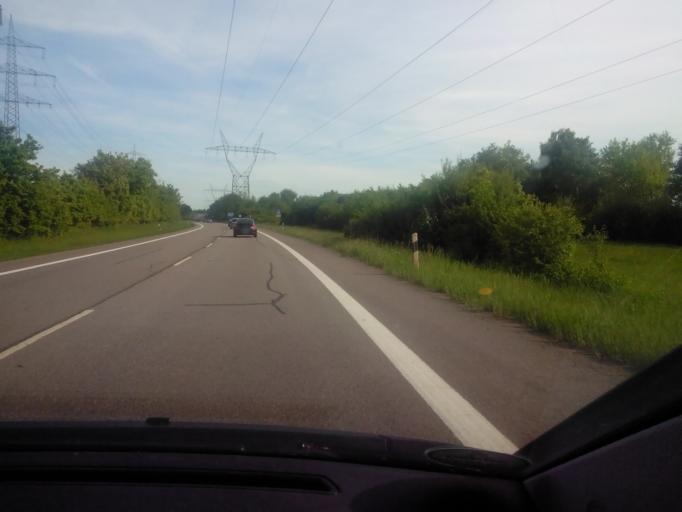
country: DE
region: Saarland
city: Nalbach
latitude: 49.3554
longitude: 6.7698
